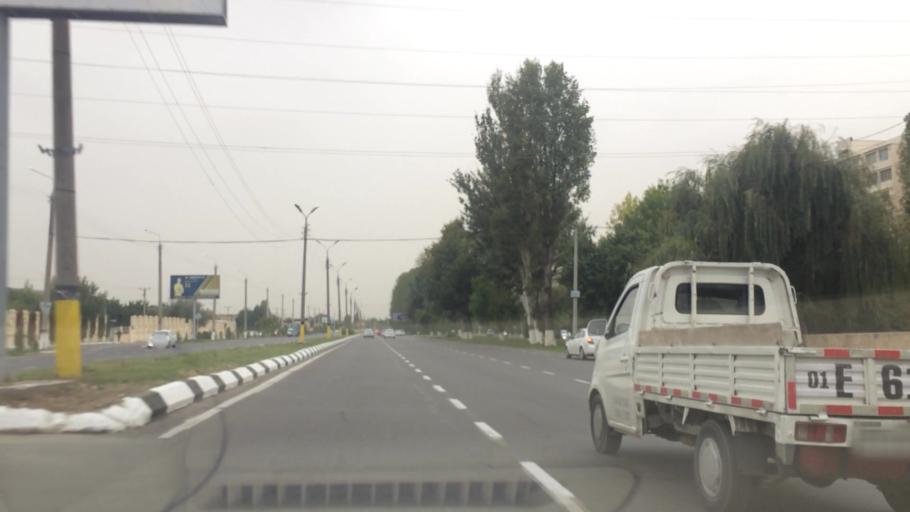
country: UZ
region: Toshkent
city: Salor
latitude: 41.3196
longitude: 69.3599
